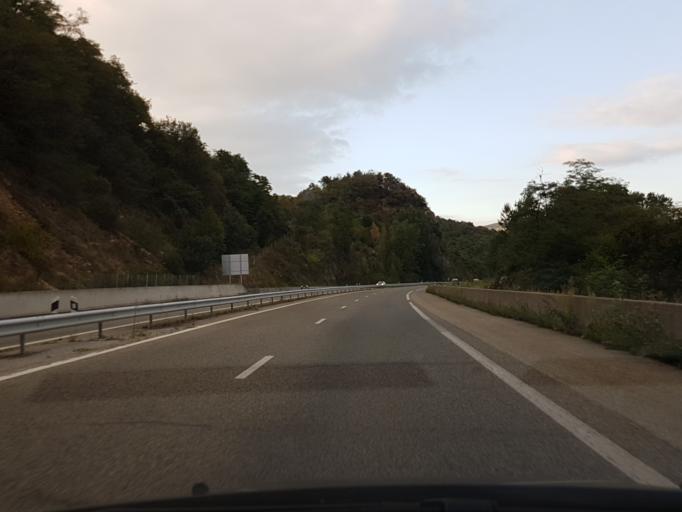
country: FR
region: Midi-Pyrenees
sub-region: Departement de l'Ariege
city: Mercus-Garrabet
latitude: 42.8940
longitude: 1.6299
